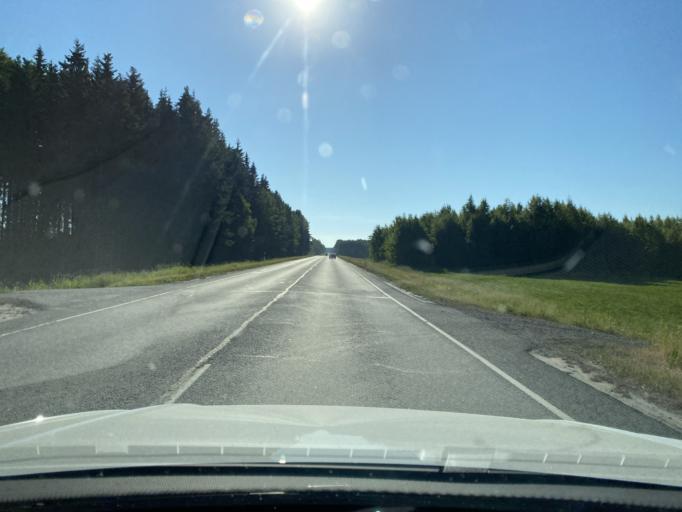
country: FI
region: Haeme
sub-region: Forssa
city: Tammela
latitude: 60.8261
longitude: 23.7548
